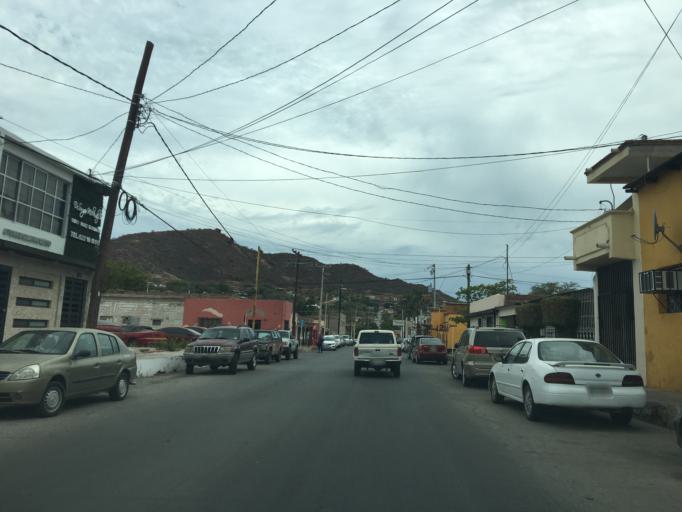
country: MX
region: Sonora
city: Heroica Guaymas
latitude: 27.9199
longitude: -110.8990
